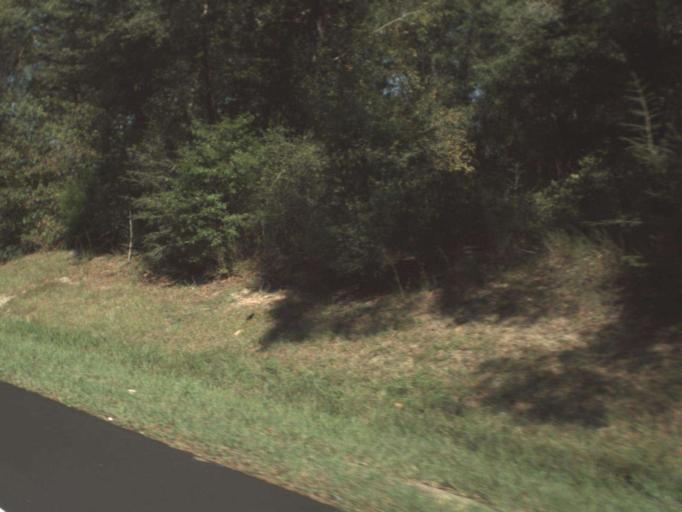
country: US
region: Florida
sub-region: Walton County
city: DeFuniak Springs
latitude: 30.8065
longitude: -86.1981
